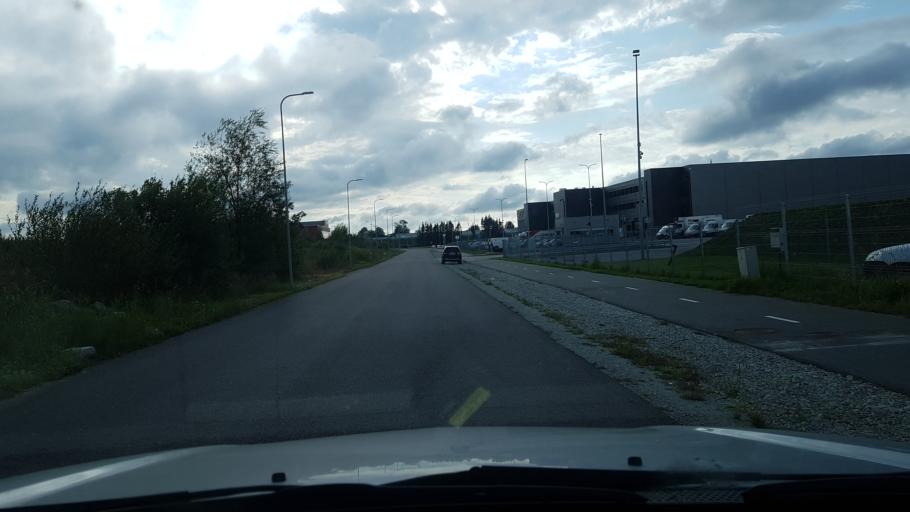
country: EE
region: Harju
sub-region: Rae vald
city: Jueri
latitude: 59.3806
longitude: 24.8498
